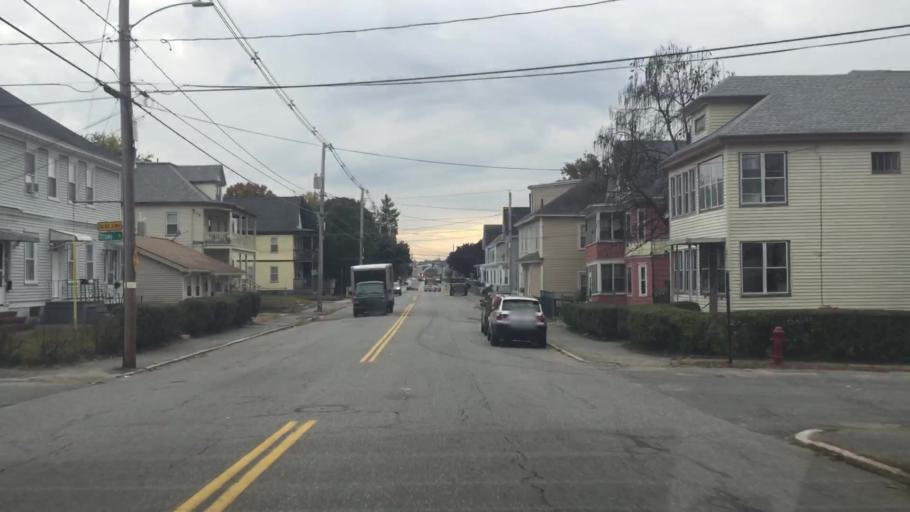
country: US
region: Massachusetts
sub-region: Middlesex County
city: Dracut
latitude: 42.6615
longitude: -71.3178
